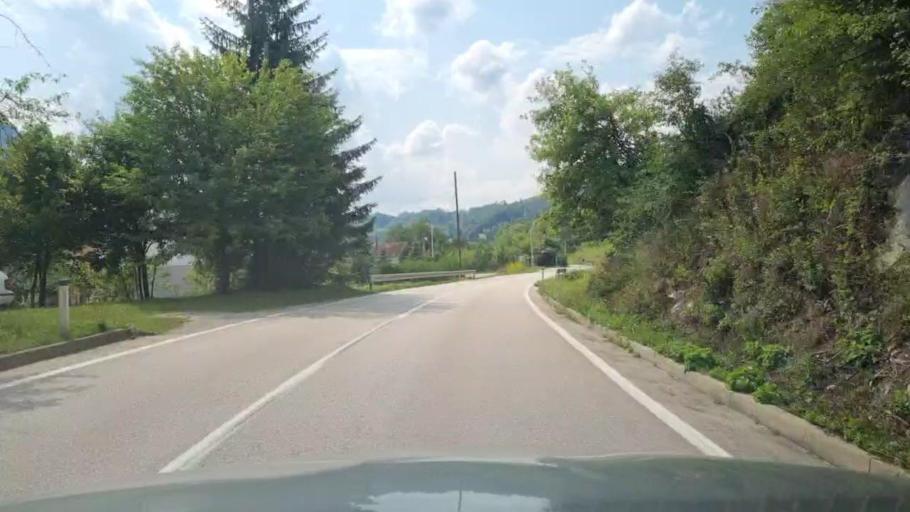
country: BA
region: Federation of Bosnia and Herzegovina
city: Kladanj
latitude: 44.2354
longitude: 18.7537
